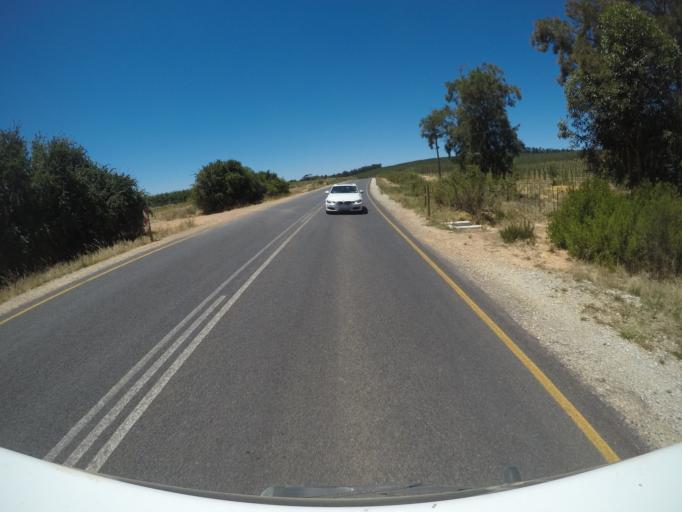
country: ZA
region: Western Cape
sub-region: Overberg District Municipality
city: Grabouw
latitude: -34.0676
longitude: 19.1203
